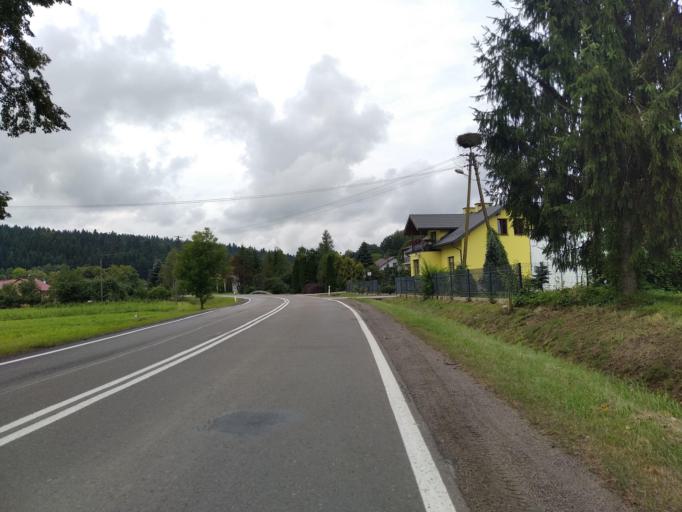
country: PL
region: Subcarpathian Voivodeship
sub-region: Powiat przemyski
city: Bircza
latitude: 49.6904
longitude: 22.4445
